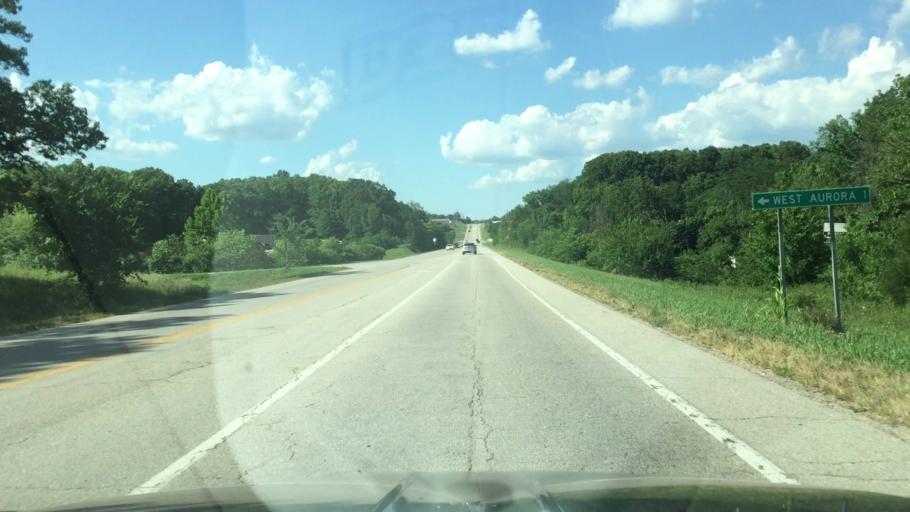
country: US
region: Missouri
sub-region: Miller County
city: Eldon
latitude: 38.3172
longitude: -92.5881
